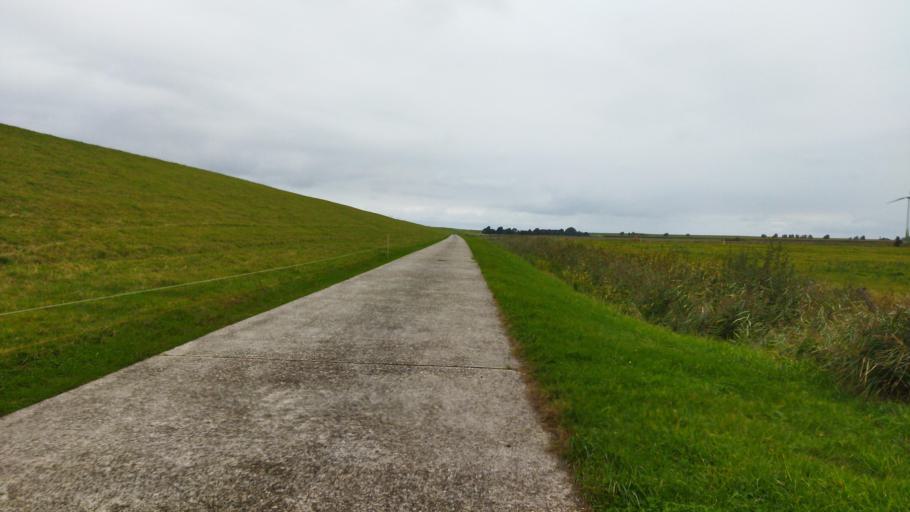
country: DE
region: Lower Saxony
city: Hinte
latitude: 53.4725
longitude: 7.0333
